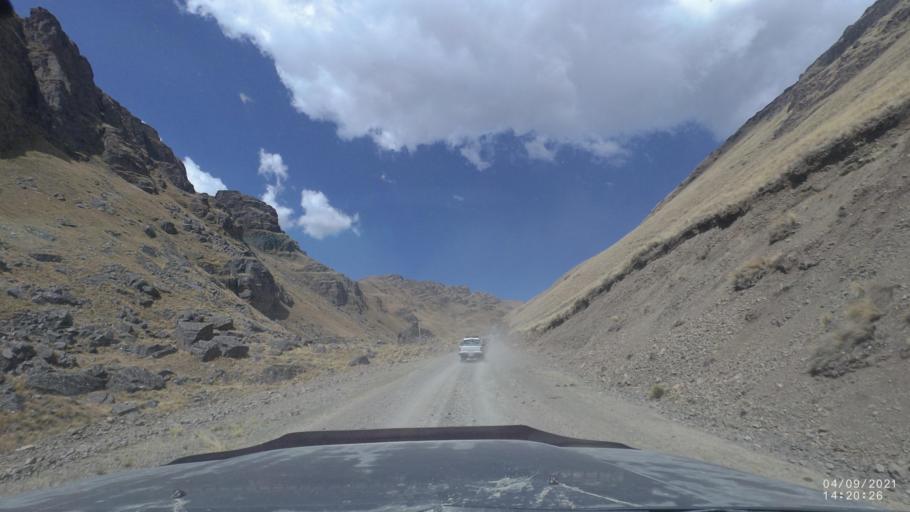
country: BO
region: Cochabamba
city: Sipe Sipe
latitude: -17.2349
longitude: -66.4202
